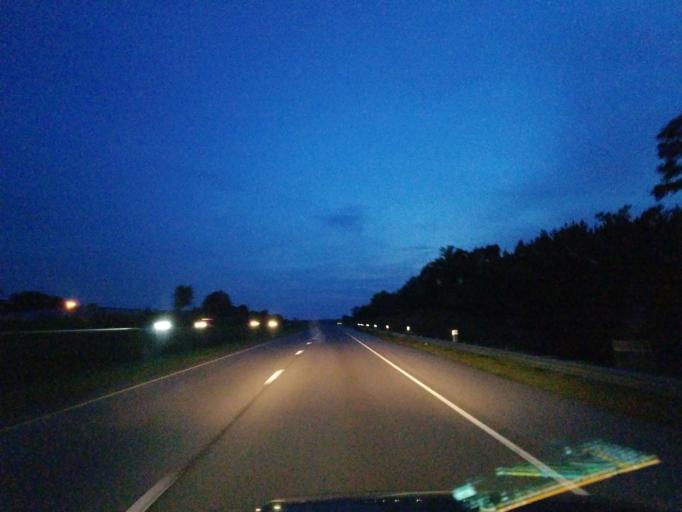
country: US
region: Mississippi
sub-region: Jones County
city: Ellisville
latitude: 31.5353
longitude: -89.2756
